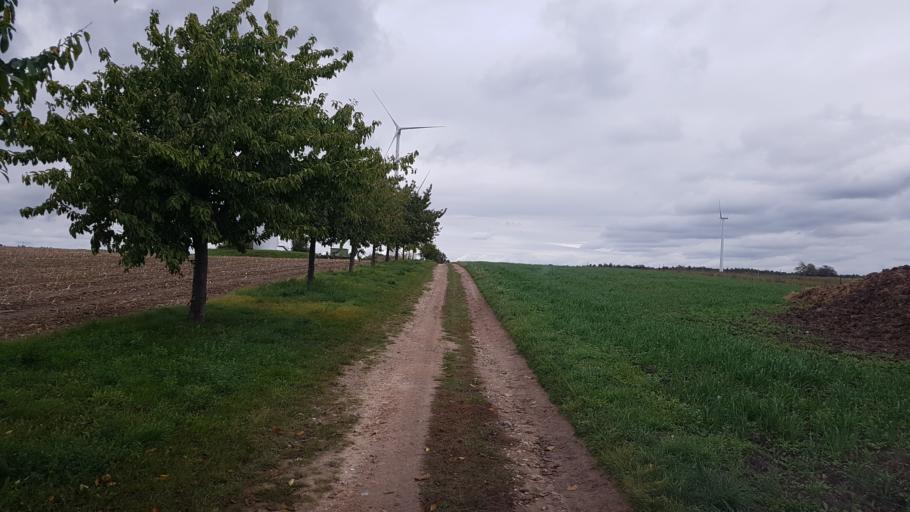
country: DE
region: Brandenburg
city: Doberlug-Kirchhain
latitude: 51.6162
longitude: 13.5931
